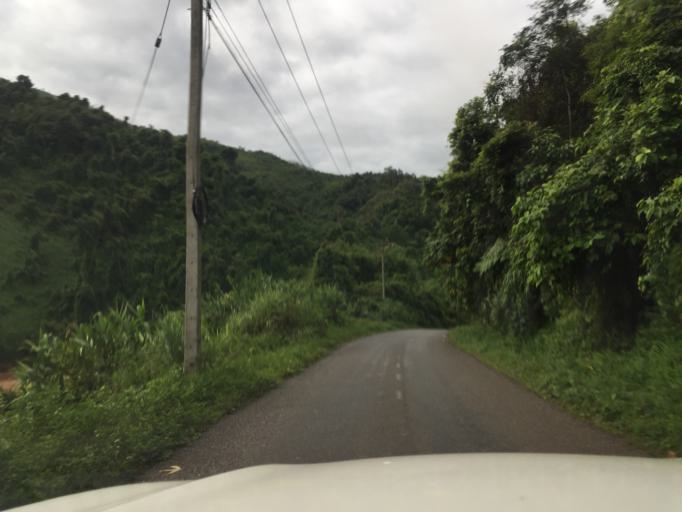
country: LA
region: Oudomxai
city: Muang La
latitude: 21.0594
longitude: 102.2413
